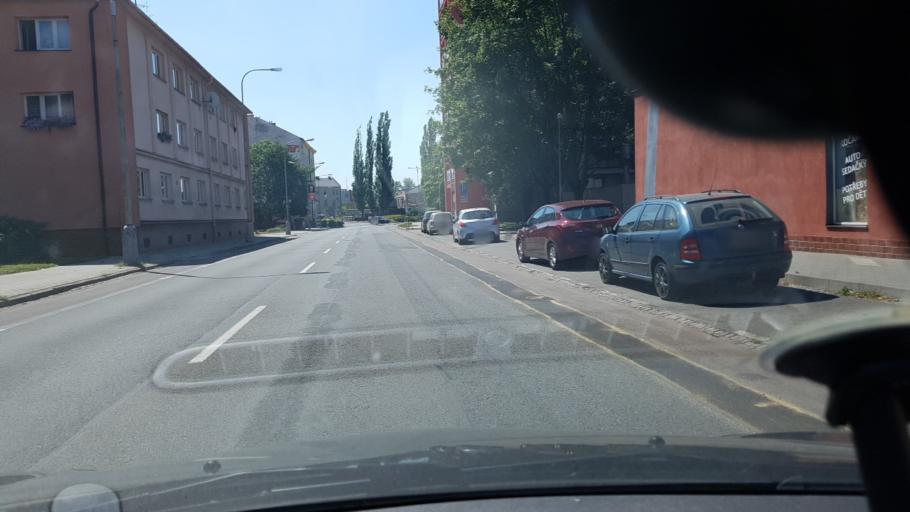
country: CZ
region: Moravskoslezsky
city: Bohumin
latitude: 49.9018
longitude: 18.3547
